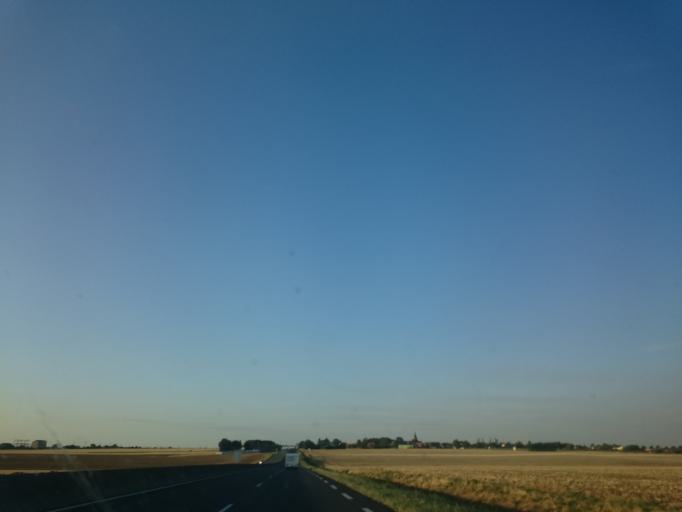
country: FR
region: Ile-de-France
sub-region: Departement de l'Essonne
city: Angerville
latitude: 48.3394
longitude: 2.0364
